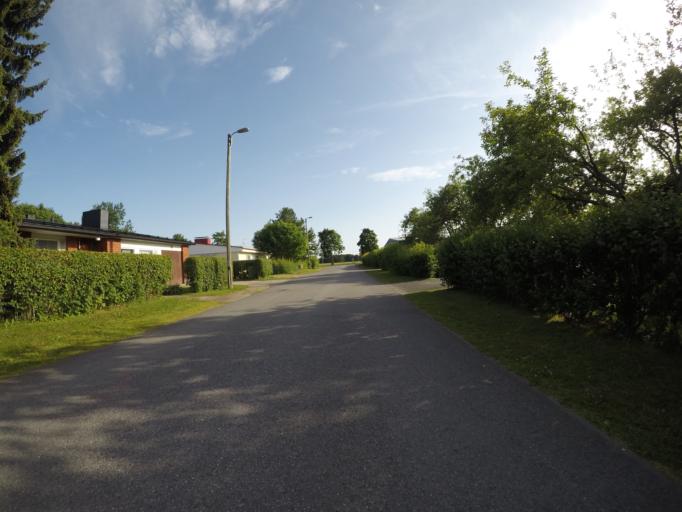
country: FI
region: Haeme
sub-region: Haemeenlinna
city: Haemeenlinna
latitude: 60.9781
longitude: 24.4199
